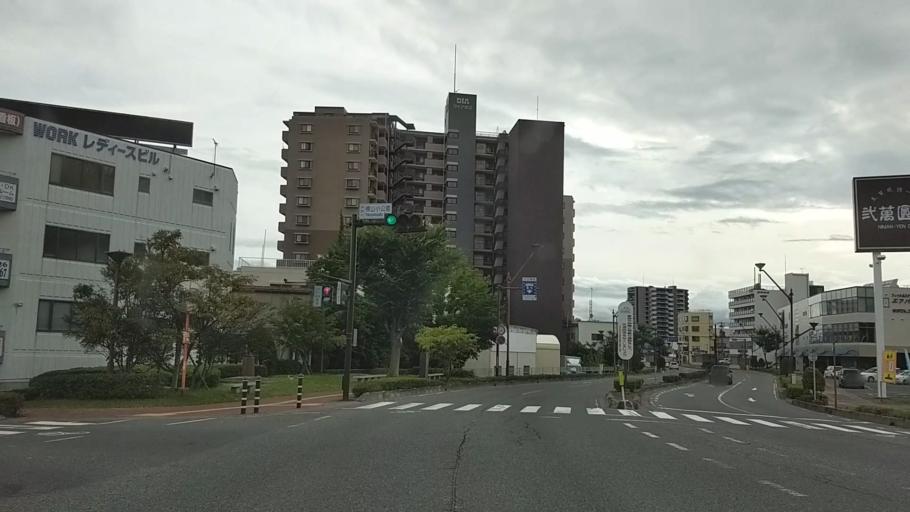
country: JP
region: Nagano
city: Nagano-shi
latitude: 36.6606
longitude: 138.1947
